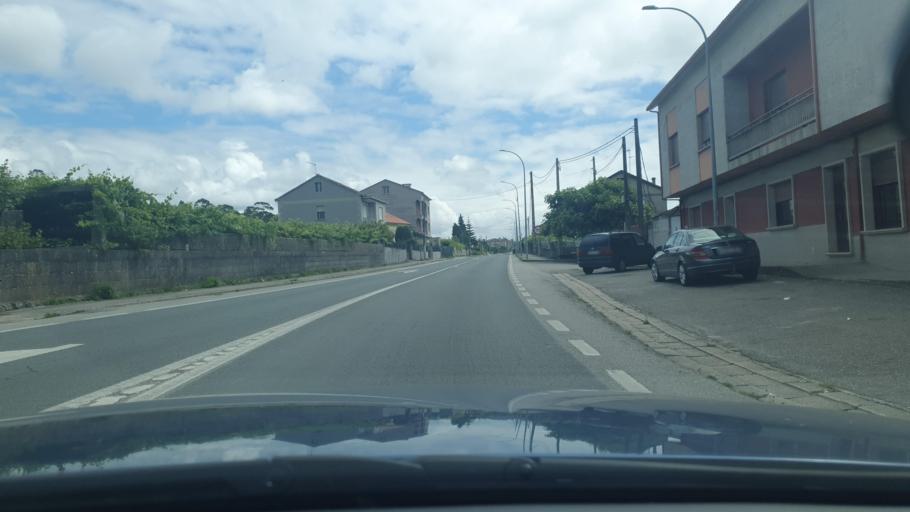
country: ES
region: Galicia
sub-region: Provincia de Pontevedra
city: Cambados
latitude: 42.4993
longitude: -8.8032
